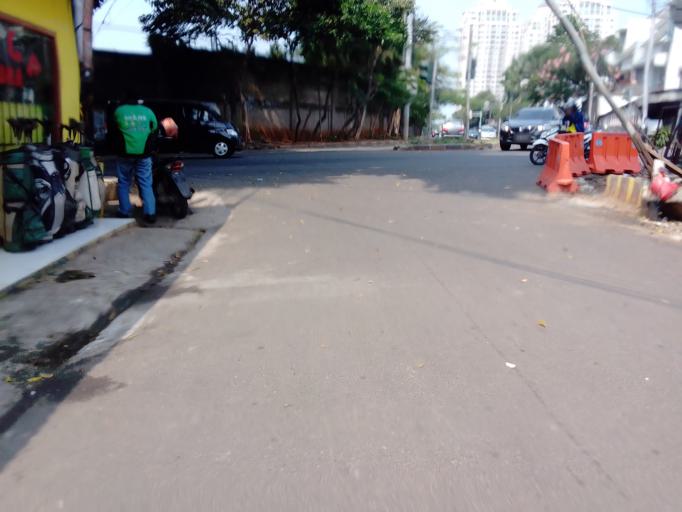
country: ID
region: Jakarta Raya
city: Jakarta
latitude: -6.2185
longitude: 106.7955
